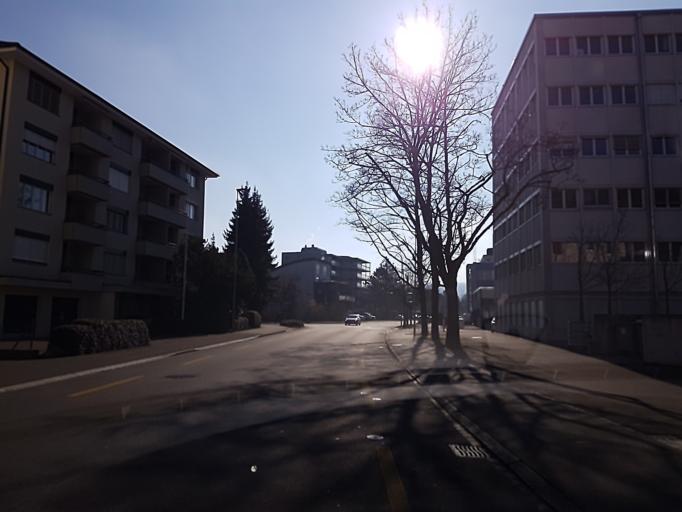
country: CH
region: Zurich
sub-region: Bezirk Dietikon
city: Dietikon / Kreuzacker
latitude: 47.4015
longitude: 8.4043
